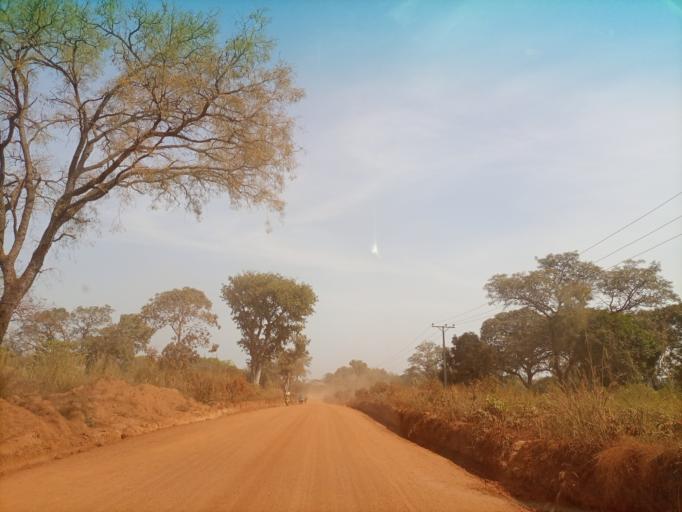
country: NG
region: Enugu
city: Eha Amufu
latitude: 6.6685
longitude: 7.7468
